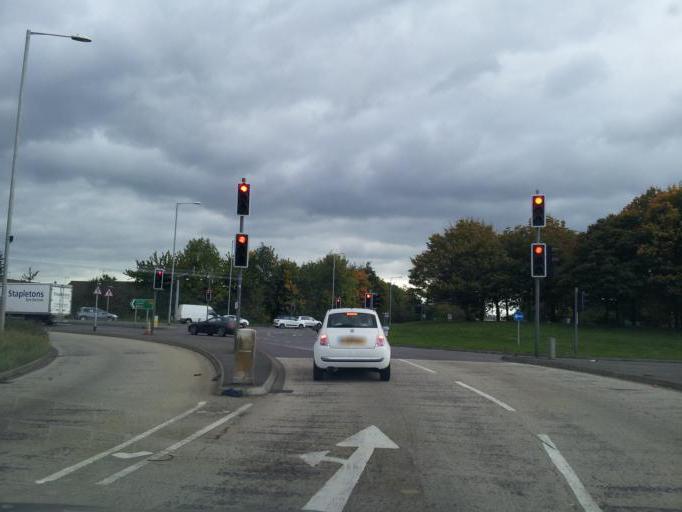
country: GB
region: England
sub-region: Northamptonshire
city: Blisworth
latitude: 52.2234
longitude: -0.9366
